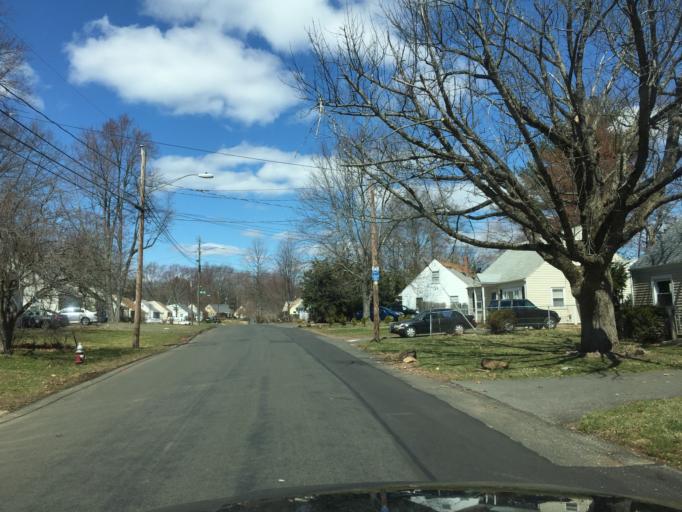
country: US
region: Connecticut
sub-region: Hartford County
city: New Britain
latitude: 41.6958
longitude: -72.7977
